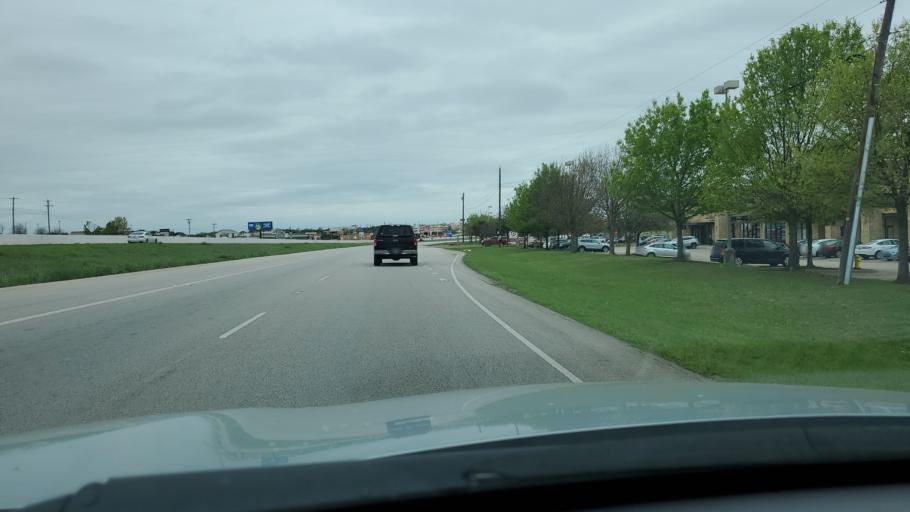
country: US
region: Texas
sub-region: Bell County
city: Harker Heights
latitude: 31.0737
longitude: -97.6593
